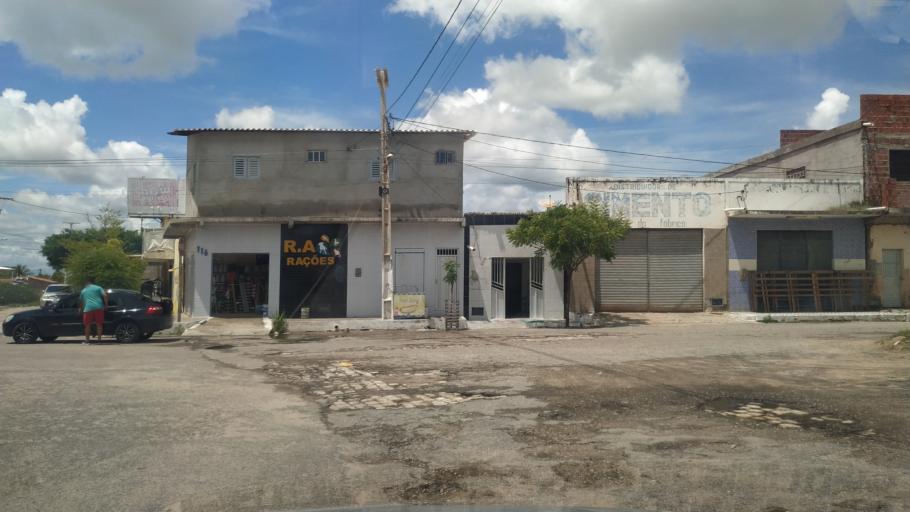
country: BR
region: Rio Grande do Norte
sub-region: Areia Branca
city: Areia Branca
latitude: -4.9550
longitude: -37.1301
